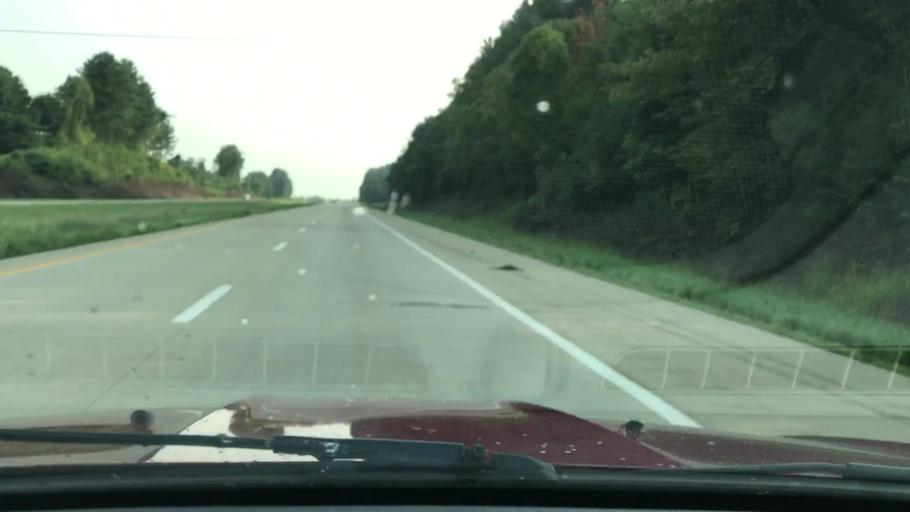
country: US
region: Ohio
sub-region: Washington County
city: Devola
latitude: 39.5200
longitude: -81.4491
